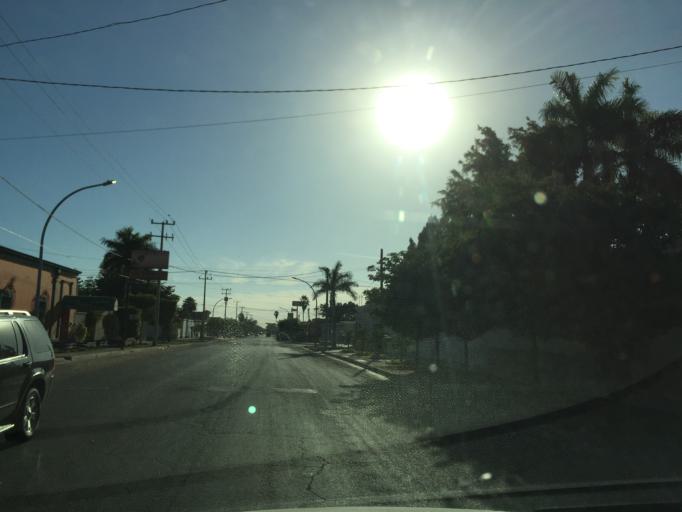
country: MX
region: Sonora
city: Navojoa
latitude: 27.0820
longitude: -109.4515
